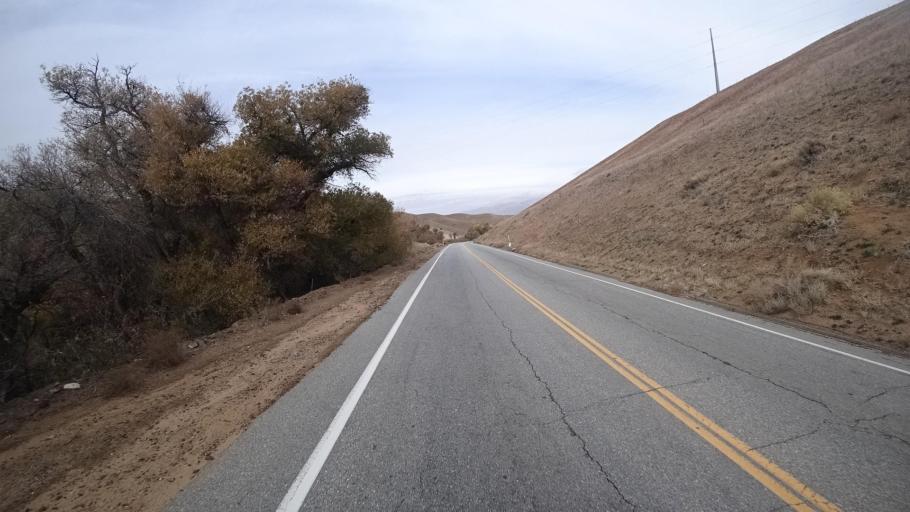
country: US
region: California
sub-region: Kern County
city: Tehachapi
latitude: 35.0658
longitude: -118.3944
